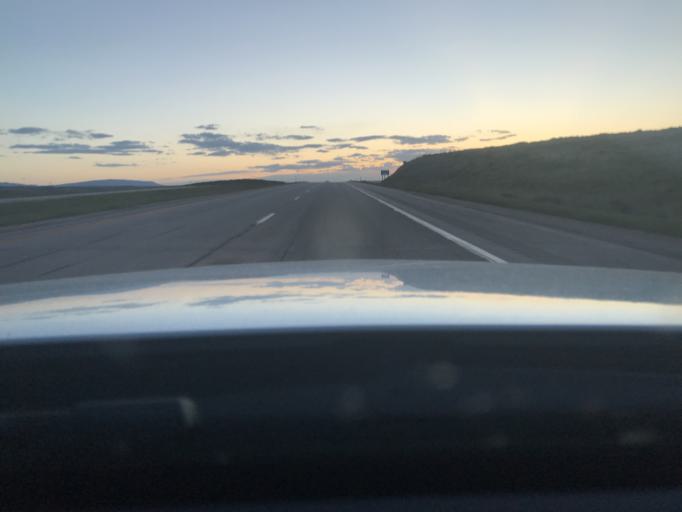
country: US
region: Wyoming
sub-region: Converse County
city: Glenrock
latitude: 42.8221
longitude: -105.7805
